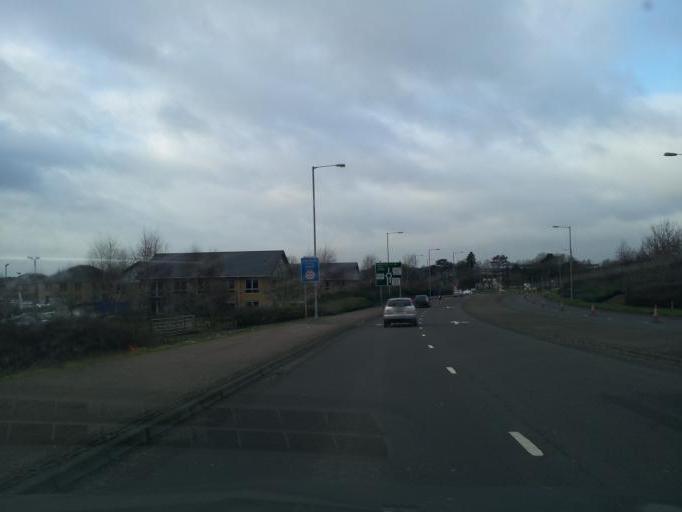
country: GB
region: England
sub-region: Norfolk
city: Surlingham
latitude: 52.6271
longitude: 1.3766
